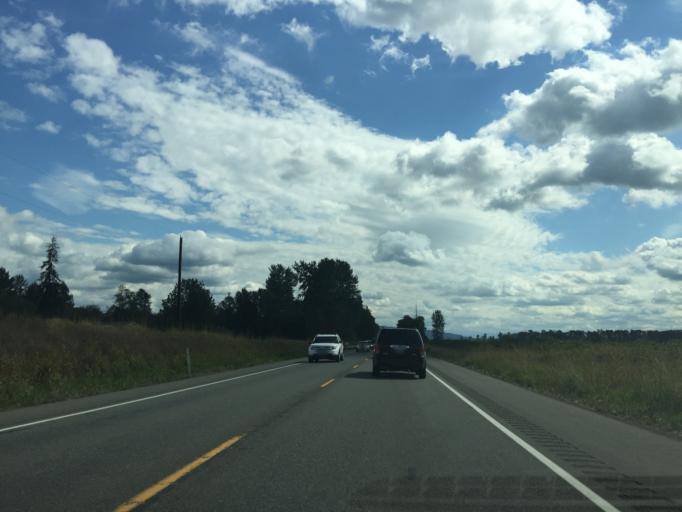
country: US
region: Washington
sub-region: Snohomish County
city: Three Lakes
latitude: 47.8949
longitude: -122.0318
